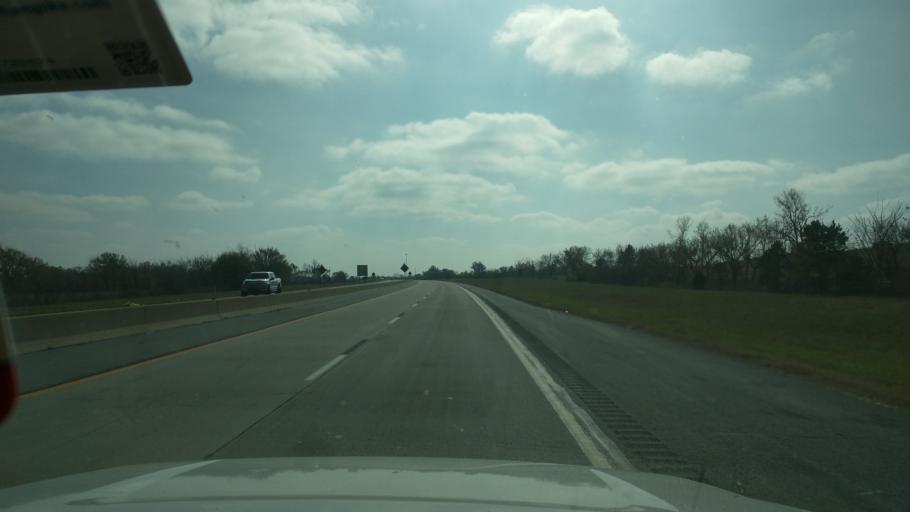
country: US
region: Oklahoma
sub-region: Wagoner County
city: Coweta
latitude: 35.9429
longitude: -95.5881
